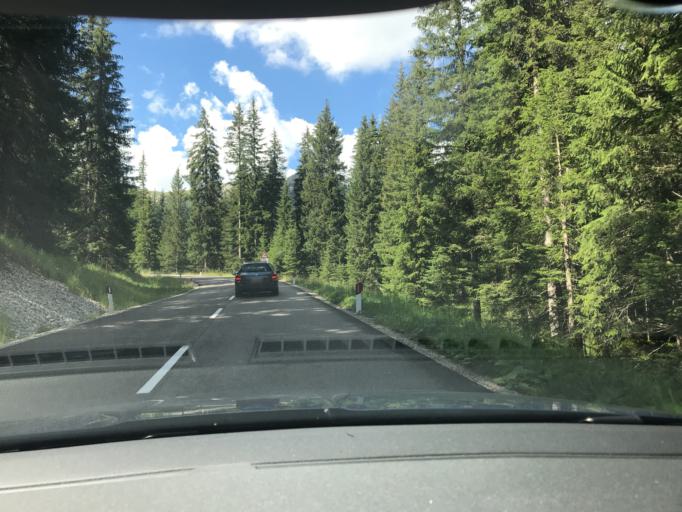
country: IT
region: Veneto
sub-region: Provincia di Belluno
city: Livinallongo del Col di Lana
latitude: 46.5514
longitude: 11.9682
